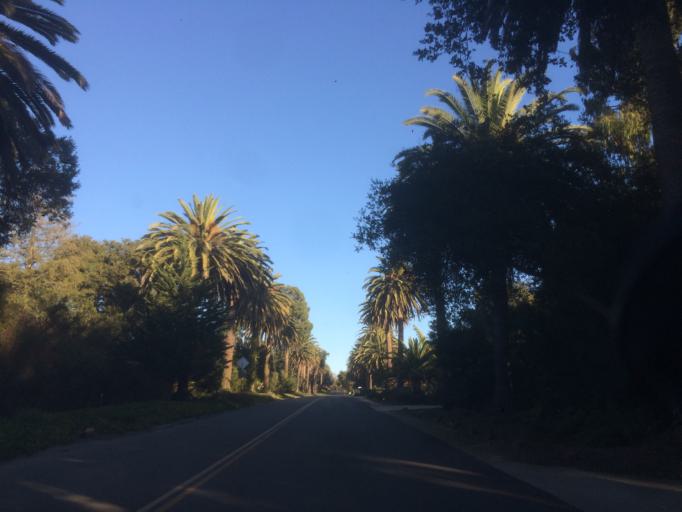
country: US
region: California
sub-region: Santa Barbara County
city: Goleta
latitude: 34.4127
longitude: -119.7714
